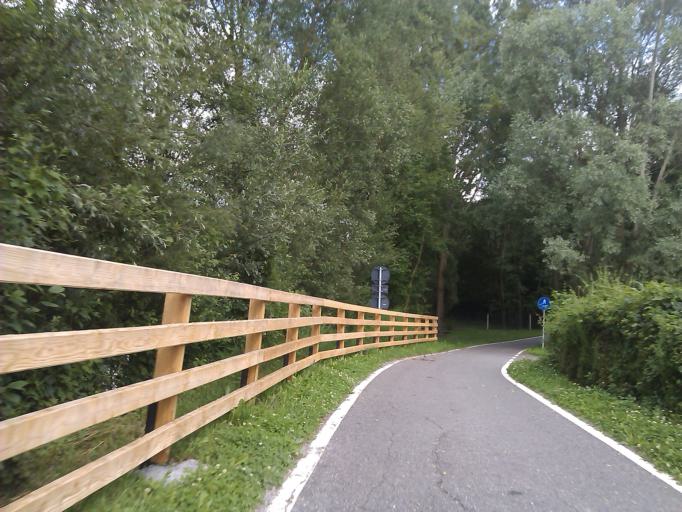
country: IT
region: Trentino-Alto Adige
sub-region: Bolzano
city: Prato Allo Stelvio
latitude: 46.6387
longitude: 10.5977
